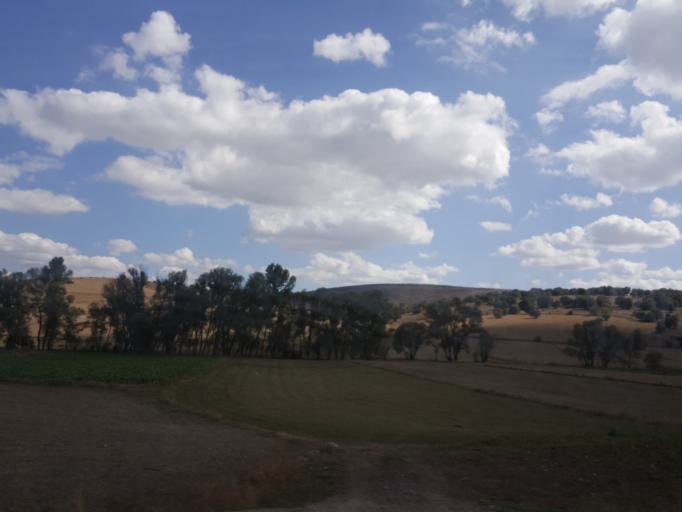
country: TR
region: Tokat
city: Camlibel
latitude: 40.1645
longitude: 36.4235
